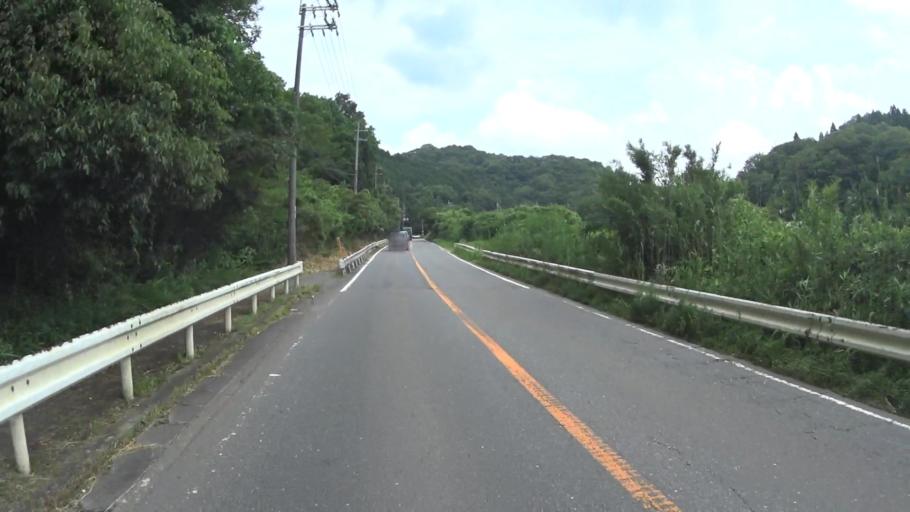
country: JP
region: Mie
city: Ueno-ebisumachi
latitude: 34.7763
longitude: 136.0099
